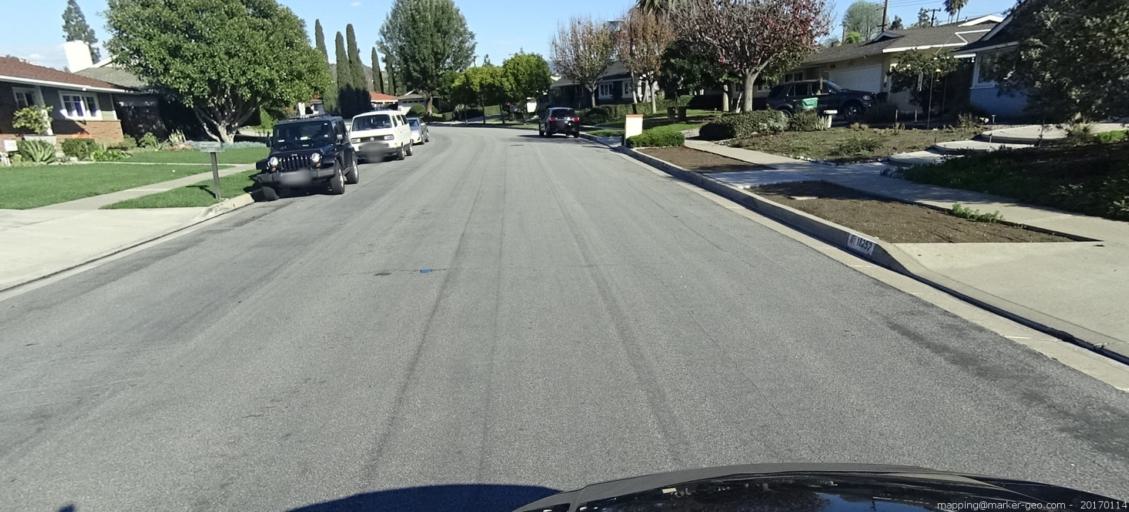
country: US
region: California
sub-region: Orange County
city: North Tustin
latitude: 33.7659
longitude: -117.8143
